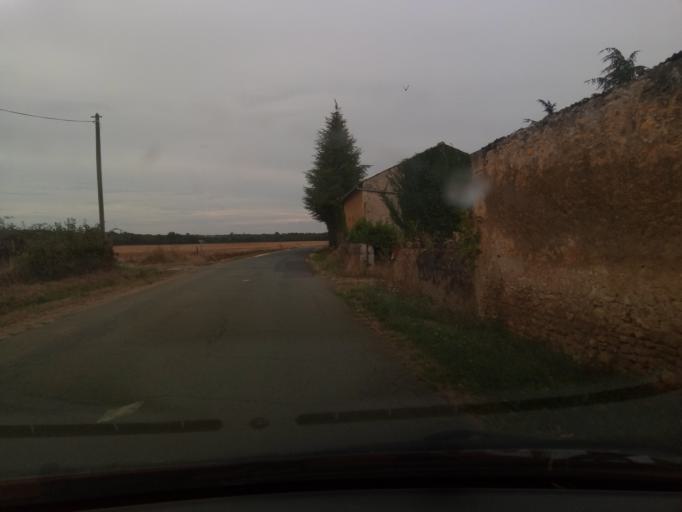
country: FR
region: Poitou-Charentes
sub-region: Departement de la Vienne
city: Saint-Savin
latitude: 46.5361
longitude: 0.7810
